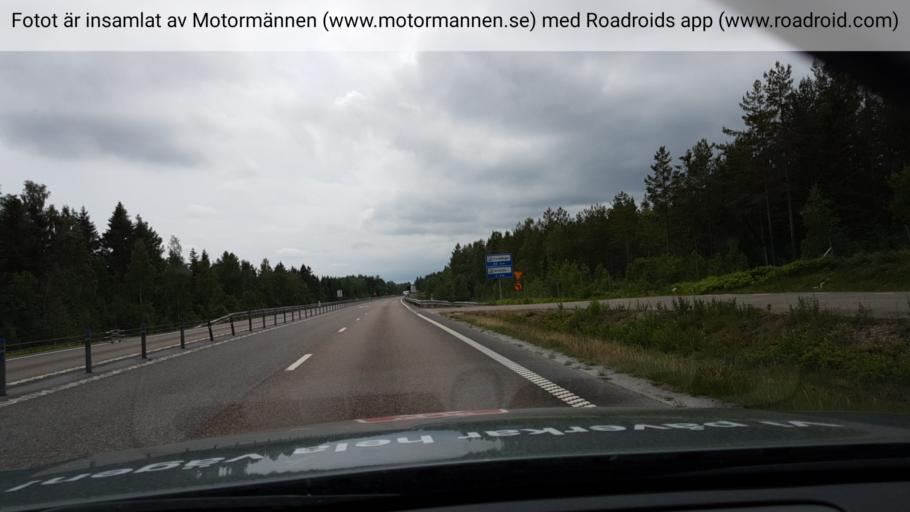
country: SE
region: Vaesternorrland
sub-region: Sundsvalls Kommun
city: Njurundabommen
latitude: 62.1755
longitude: 17.3569
